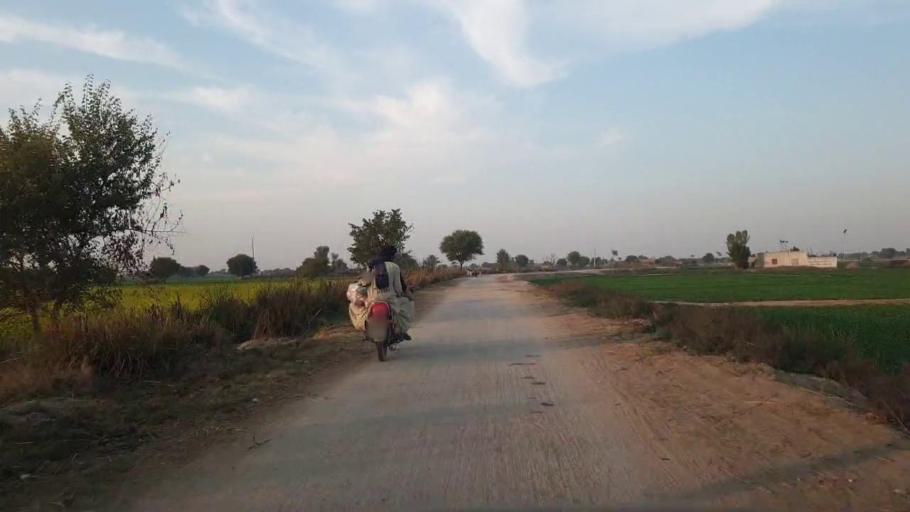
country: PK
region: Sindh
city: Shahpur Chakar
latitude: 26.1891
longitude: 68.6169
